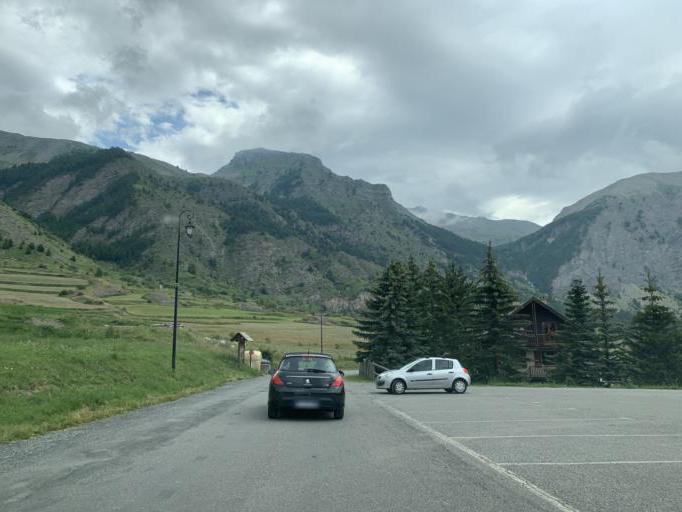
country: FR
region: Provence-Alpes-Cote d'Azur
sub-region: Departement des Hautes-Alpes
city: Guillestre
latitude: 44.5480
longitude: 6.6238
